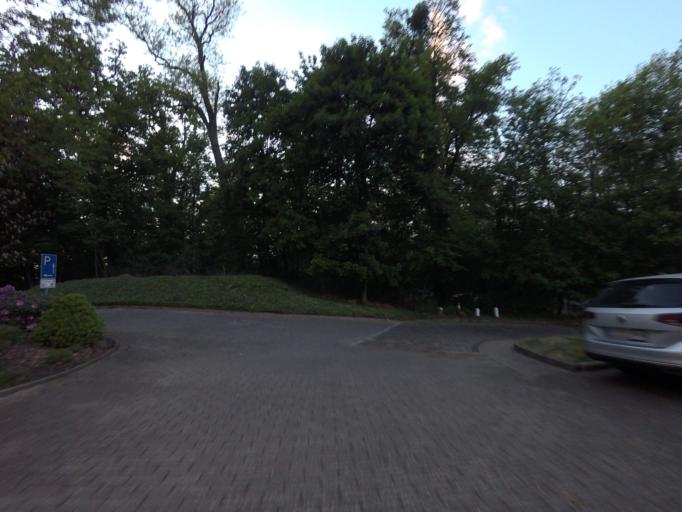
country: DE
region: Lower Saxony
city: Hildesheim
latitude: 52.1456
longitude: 9.9271
